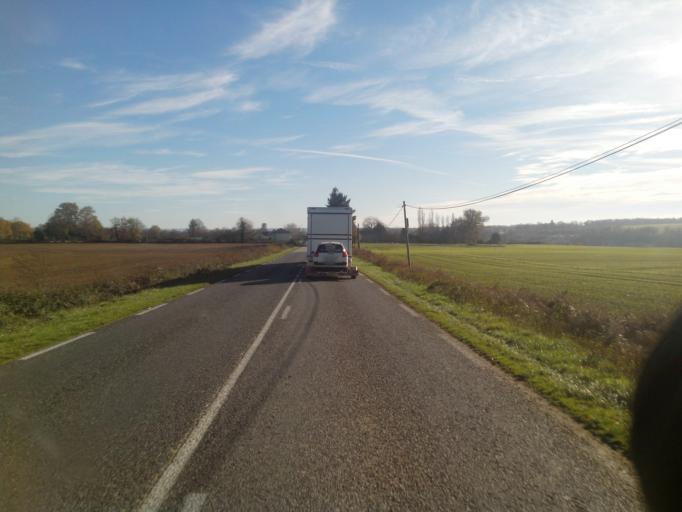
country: FR
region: Limousin
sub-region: Departement de la Haute-Vienne
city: Bellac
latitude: 46.0747
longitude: 1.0981
